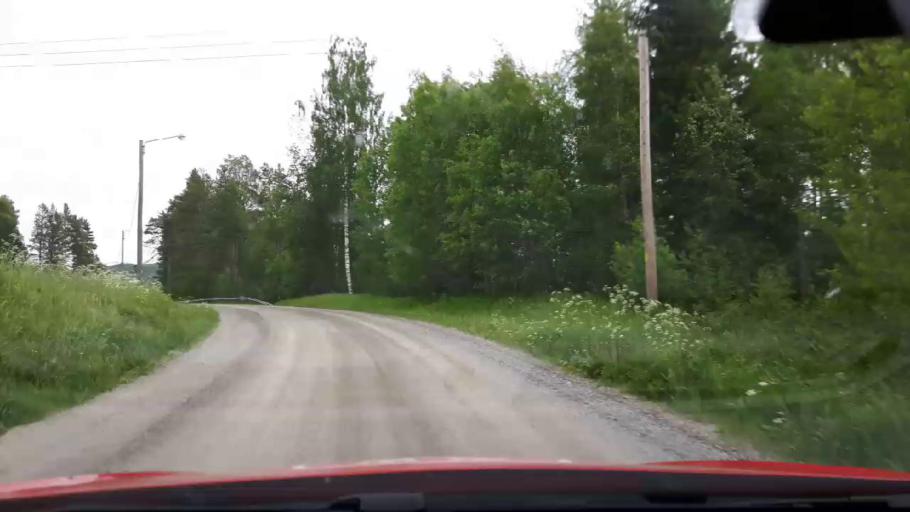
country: SE
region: Jaemtland
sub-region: Ragunda Kommun
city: Hammarstrand
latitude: 63.1585
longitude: 16.2268
